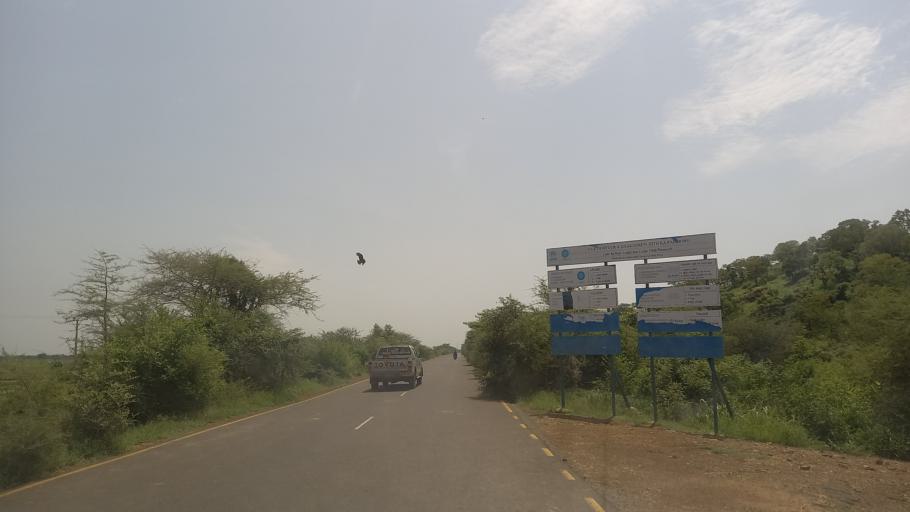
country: ET
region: Gambela
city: Gambela
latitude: 8.2848
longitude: 34.2118
